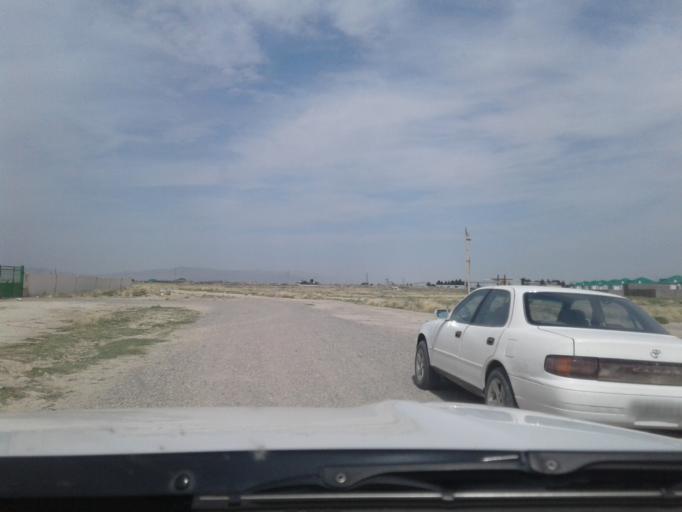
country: TM
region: Balkan
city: Serdar
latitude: 38.9960
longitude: 56.2683
